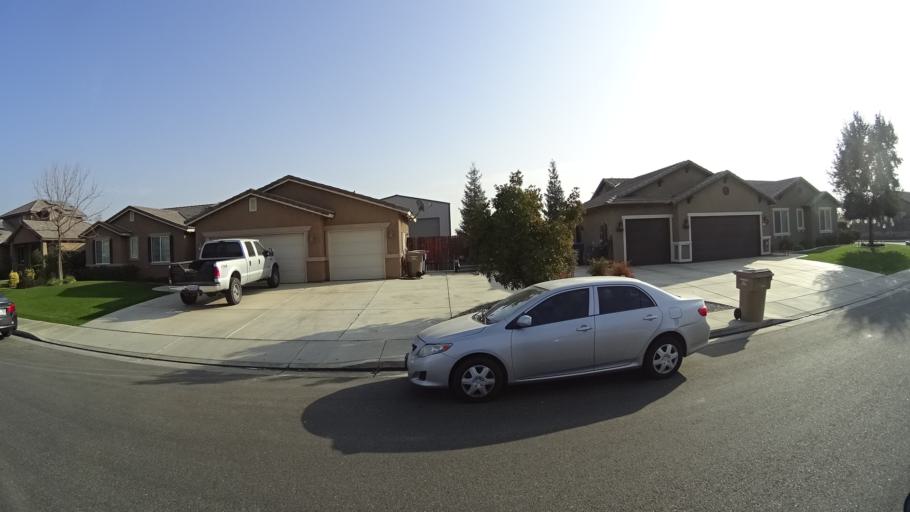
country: US
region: California
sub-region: Kern County
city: Greenacres
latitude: 35.4314
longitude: -119.1197
